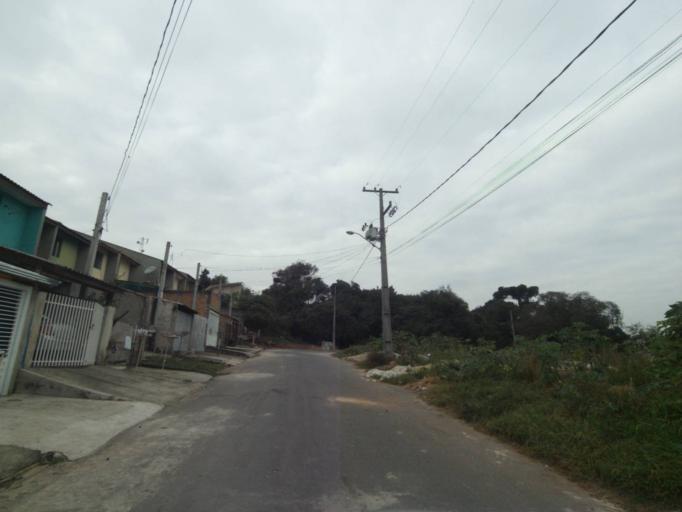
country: BR
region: Parana
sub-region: Curitiba
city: Curitiba
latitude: -25.5150
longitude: -49.3229
